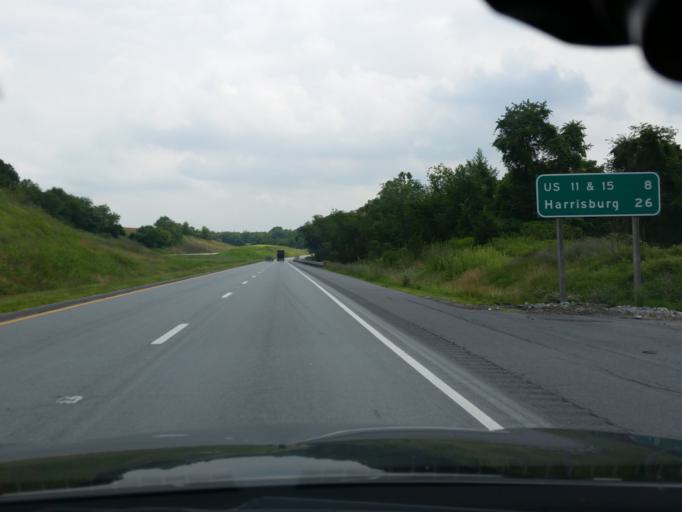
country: US
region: Pennsylvania
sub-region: Perry County
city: Newport
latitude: 40.4938
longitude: -77.0900
